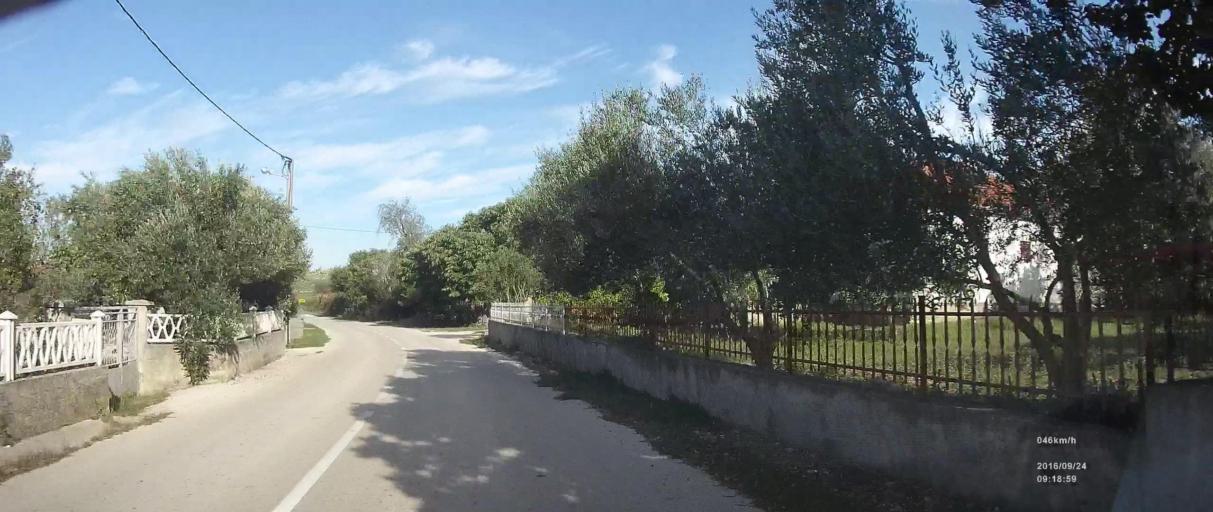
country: HR
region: Zadarska
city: Polaca
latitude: 44.0594
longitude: 15.5081
